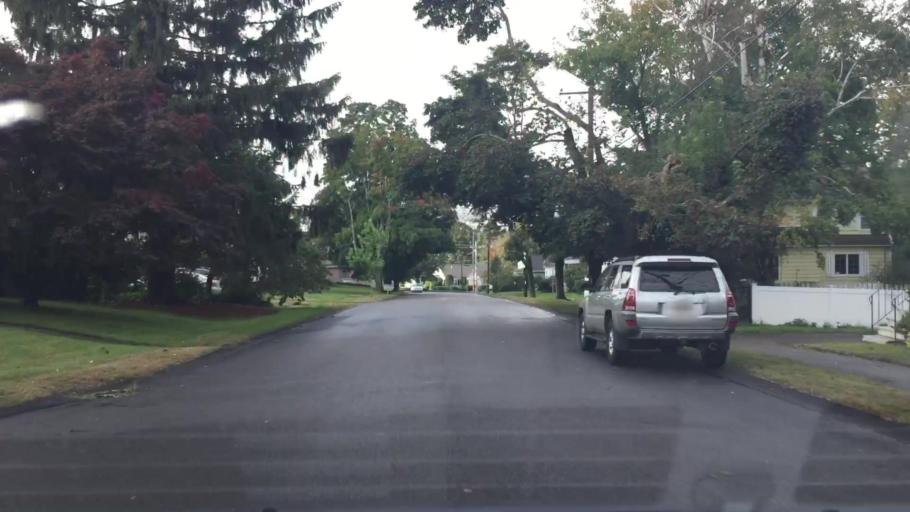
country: US
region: Massachusetts
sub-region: Essex County
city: North Andover
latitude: 42.6953
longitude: -71.1331
